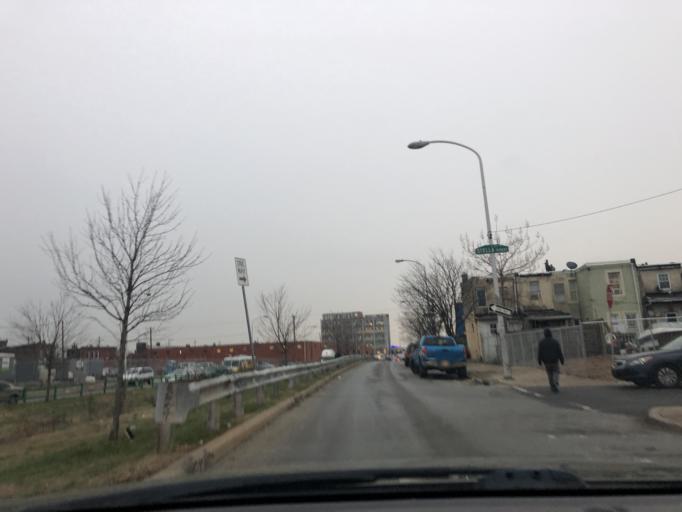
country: US
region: Pennsylvania
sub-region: Philadelphia County
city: Philadelphia
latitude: 39.9959
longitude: -75.1355
